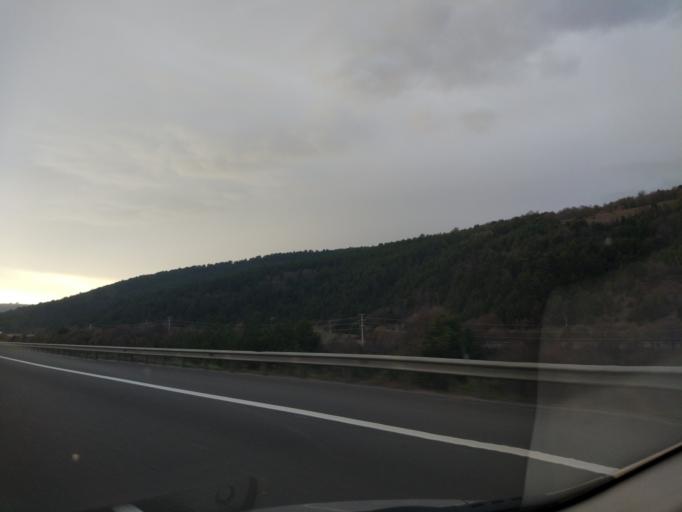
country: TR
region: Bolu
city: Gokcesu
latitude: 40.7396
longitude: 31.8357
